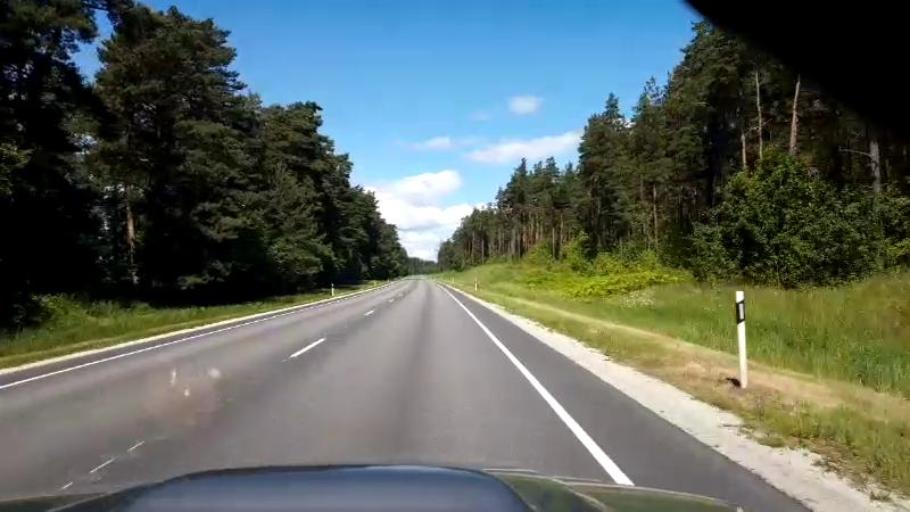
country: EE
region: Paernumaa
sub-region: Paernu linn
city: Parnu
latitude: 58.1729
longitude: 24.4946
